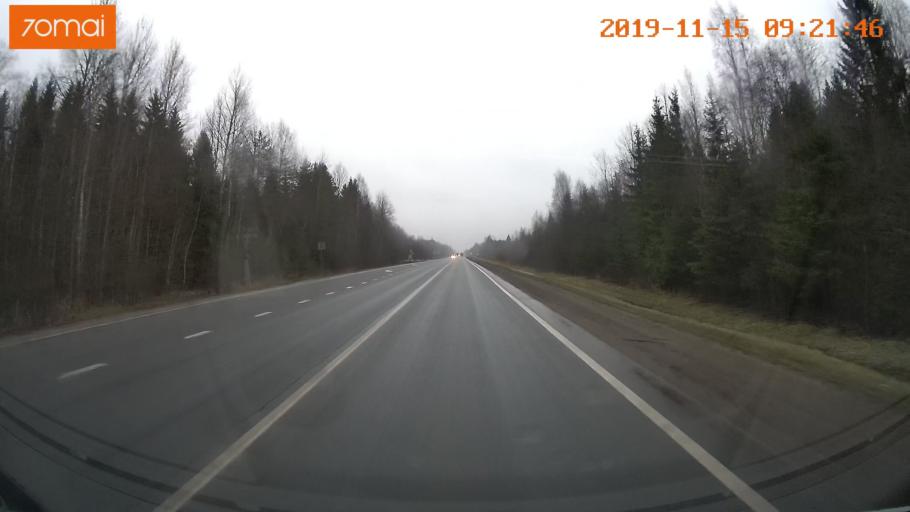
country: RU
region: Vologda
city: Tonshalovo
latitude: 59.2956
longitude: 38.0724
